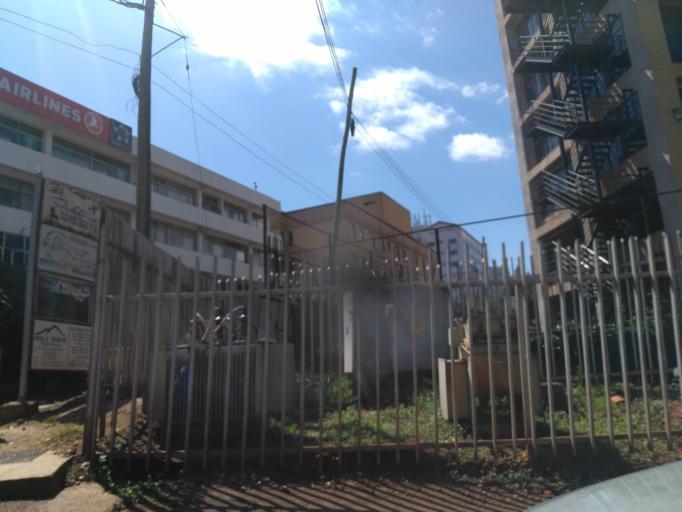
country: UG
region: Central Region
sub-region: Kampala District
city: Kampala
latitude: 0.3203
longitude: 32.5885
